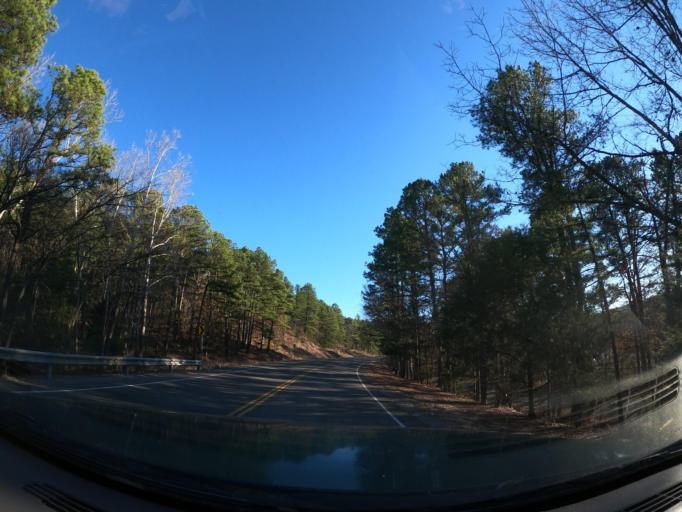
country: US
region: Oklahoma
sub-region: Latimer County
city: Wilburton
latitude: 34.9726
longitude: -95.3557
